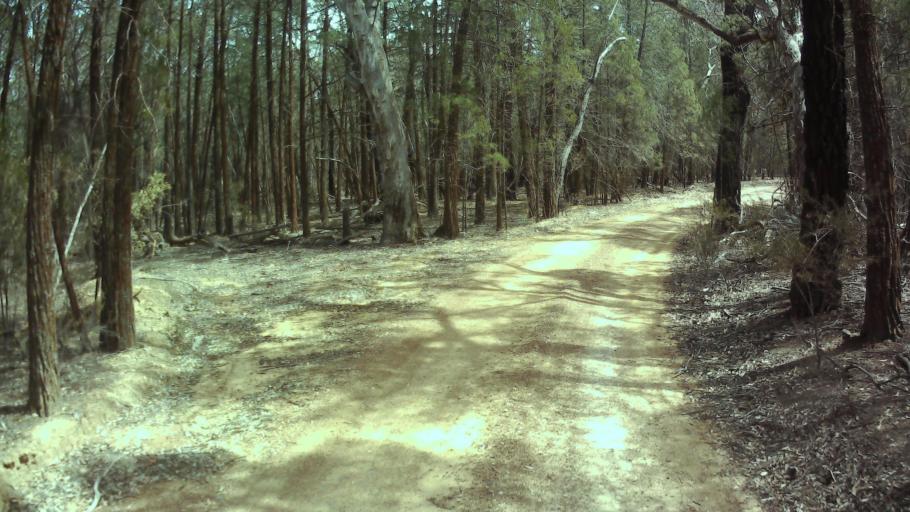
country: AU
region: New South Wales
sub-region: Weddin
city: Grenfell
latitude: -33.8881
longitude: 148.3830
